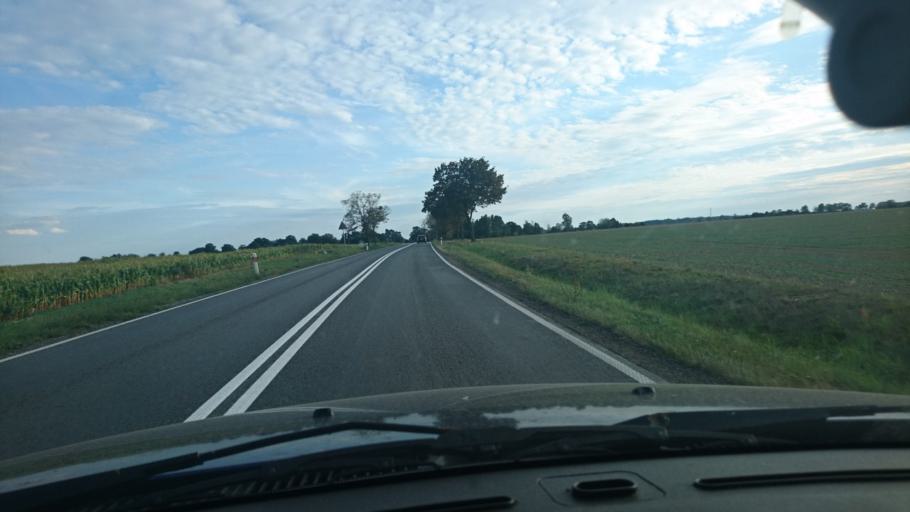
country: PL
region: Opole Voivodeship
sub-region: Powiat kluczborski
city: Byczyna
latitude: 51.0687
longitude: 18.2037
